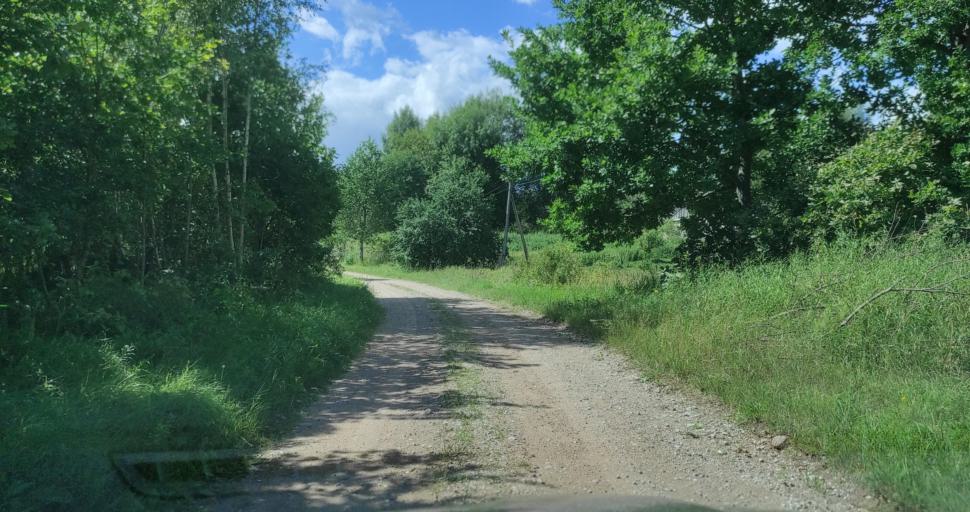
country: LV
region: Alsunga
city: Alsunga
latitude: 57.0276
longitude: 21.6974
